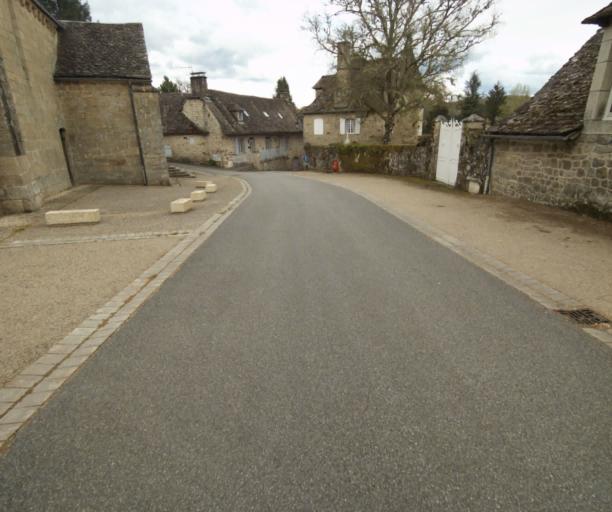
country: FR
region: Limousin
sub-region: Departement de la Correze
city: Argentat
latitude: 45.1958
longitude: 1.9710
